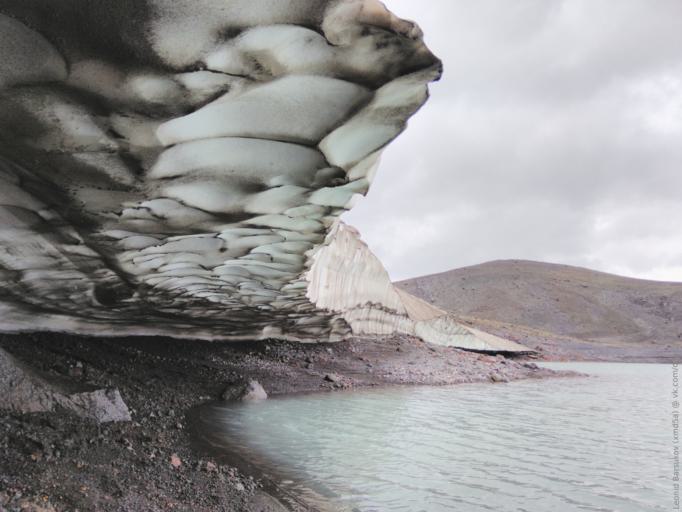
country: RU
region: Kabardino-Balkariya
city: Terskol
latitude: 43.3805
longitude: 42.5392
